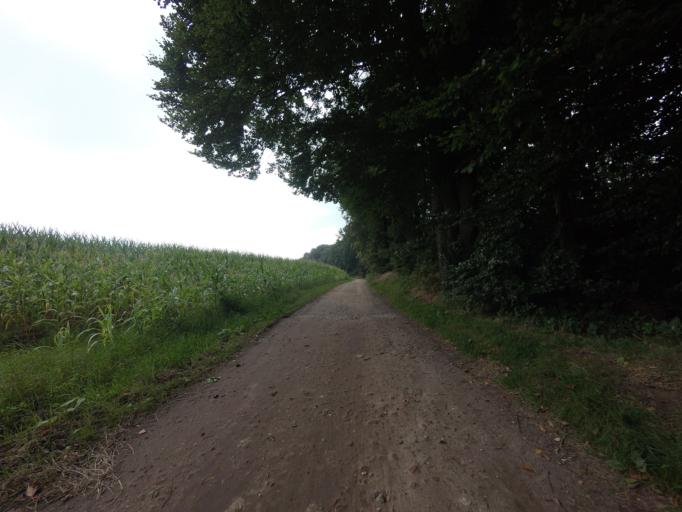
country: DE
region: Lower Saxony
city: Getelo
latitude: 52.4507
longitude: 6.8683
